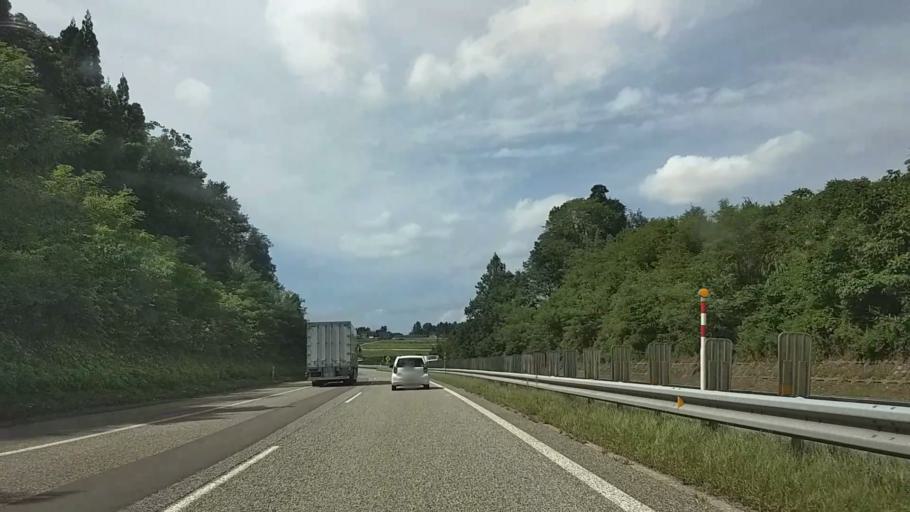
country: JP
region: Toyama
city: Takaoka
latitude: 36.6816
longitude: 137.0479
